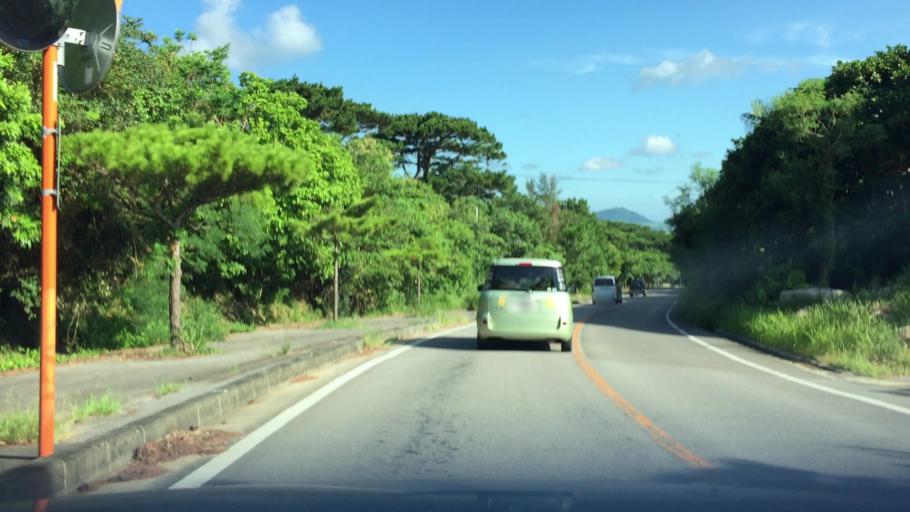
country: JP
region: Okinawa
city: Ishigaki
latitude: 24.4387
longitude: 124.1191
